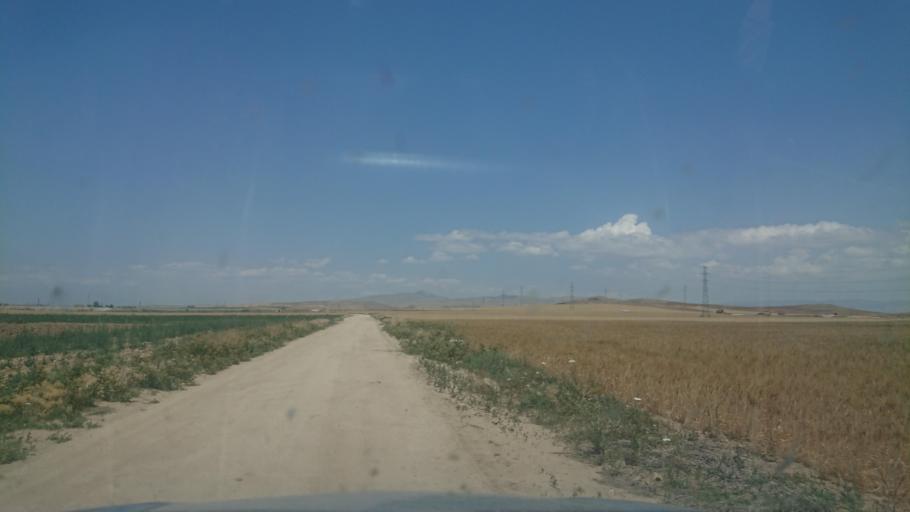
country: TR
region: Aksaray
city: Sariyahsi
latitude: 39.0153
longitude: 33.8761
